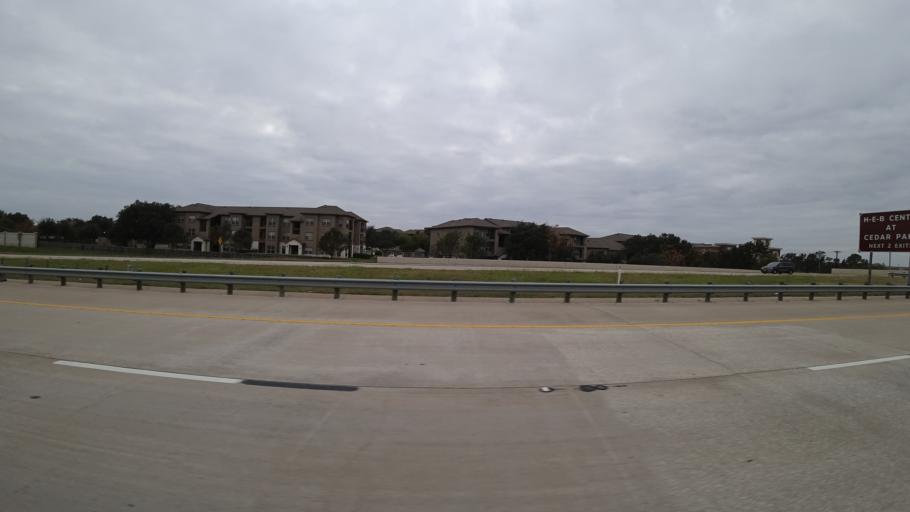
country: US
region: Texas
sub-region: Williamson County
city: Cedar Park
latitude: 30.5227
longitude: -97.8156
